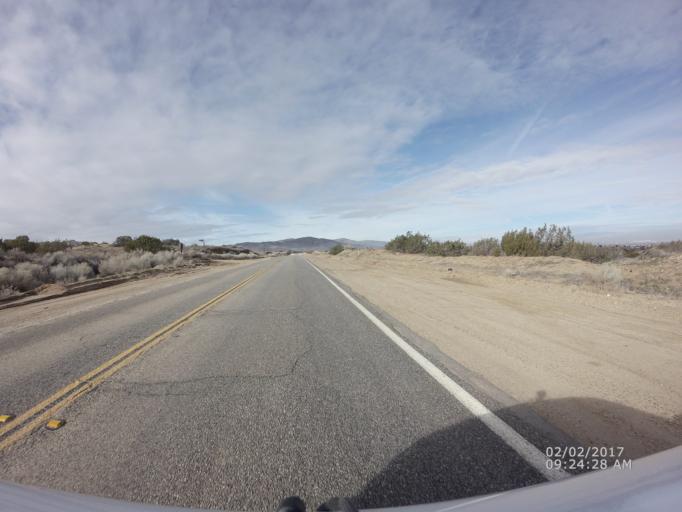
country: US
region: California
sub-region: Los Angeles County
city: Vincent
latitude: 34.5283
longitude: -118.0624
